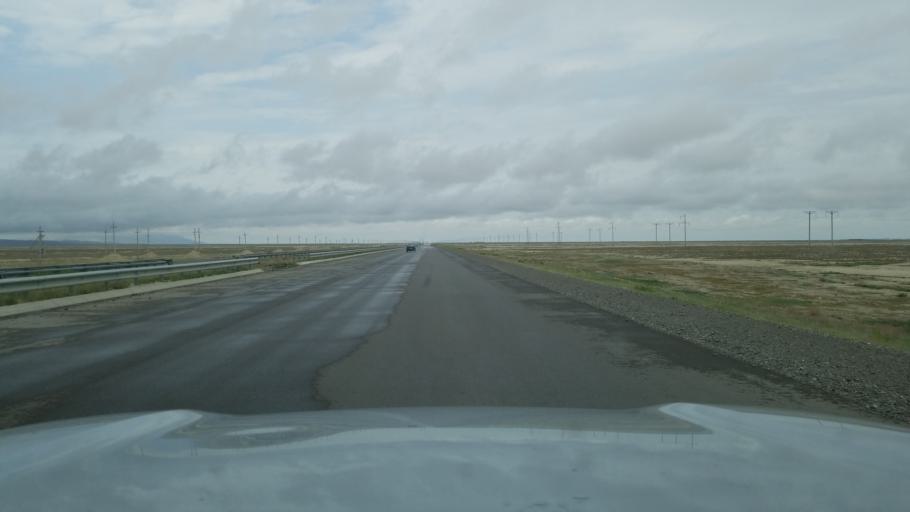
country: TM
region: Balkan
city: Serdar
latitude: 39.1211
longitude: 55.9064
